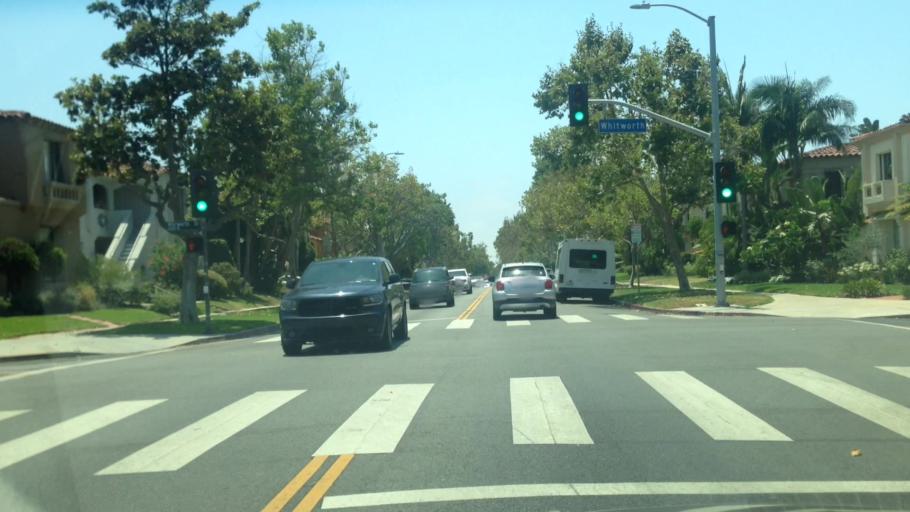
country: US
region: California
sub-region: Los Angeles County
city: West Hollywood
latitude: 34.0566
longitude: -118.3703
